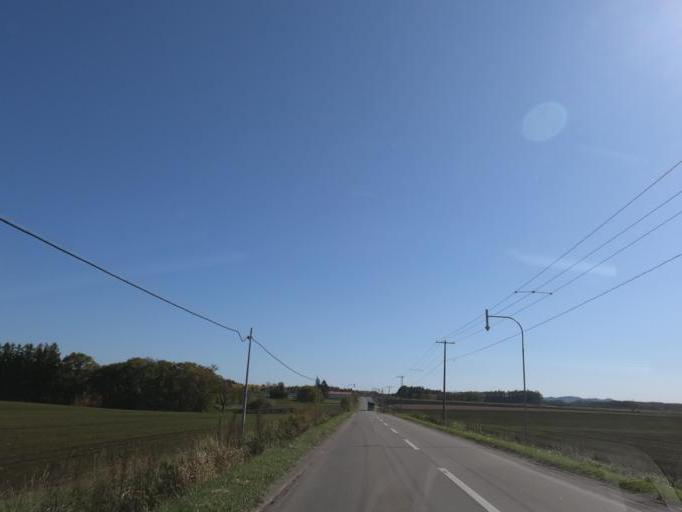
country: JP
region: Hokkaido
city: Obihiro
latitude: 42.8068
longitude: 143.2553
